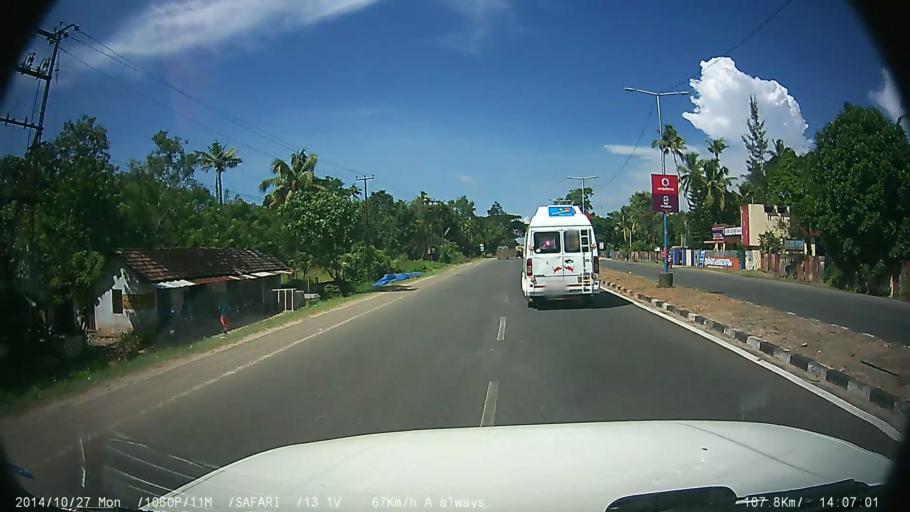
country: IN
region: Kerala
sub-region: Alappuzha
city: Kutiatodu
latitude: 9.7552
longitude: 76.3183
